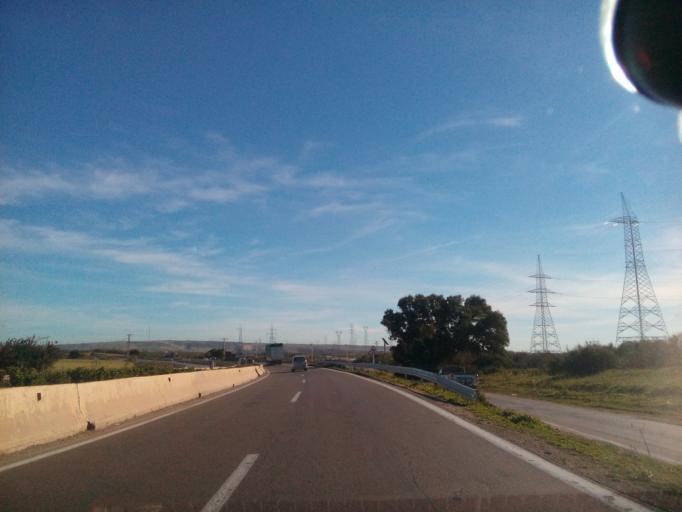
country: DZ
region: Oran
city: Ain el Bya
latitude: 35.7823
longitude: -0.1350
